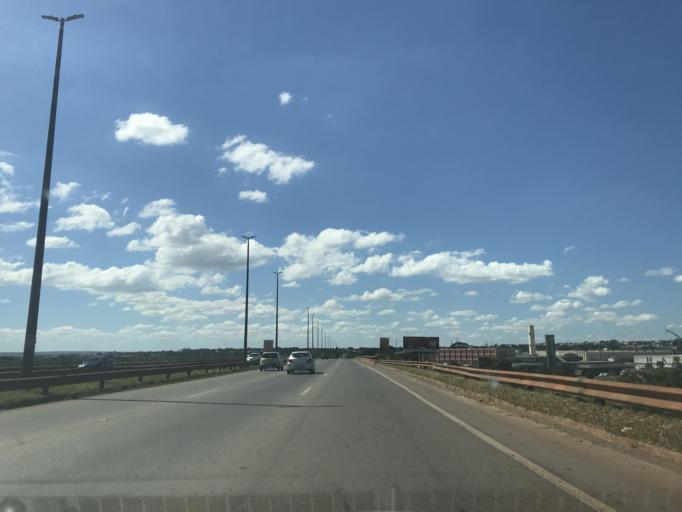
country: BR
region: Federal District
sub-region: Brasilia
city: Brasilia
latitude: -15.7905
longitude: -47.9513
